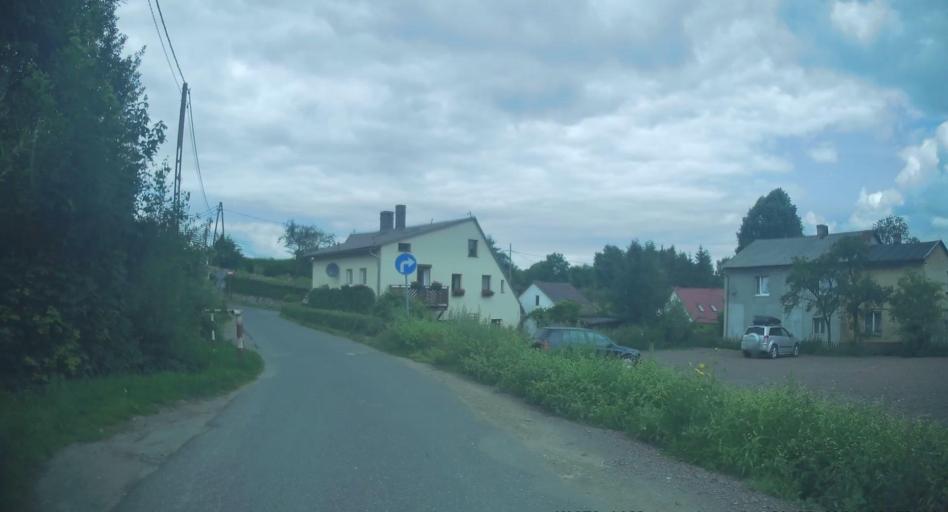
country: PL
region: Lower Silesian Voivodeship
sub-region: Powiat kamiennogorski
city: Marciszow
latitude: 50.8350
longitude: 15.9742
